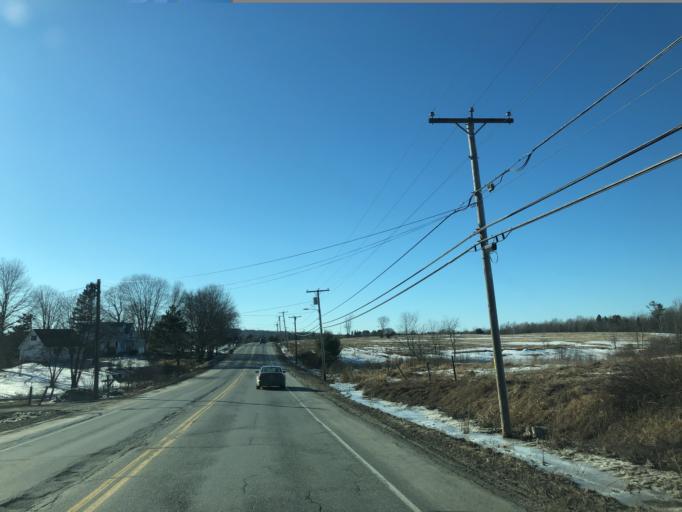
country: US
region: Maine
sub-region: Penobscot County
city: Bangor
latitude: 44.8540
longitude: -68.8145
